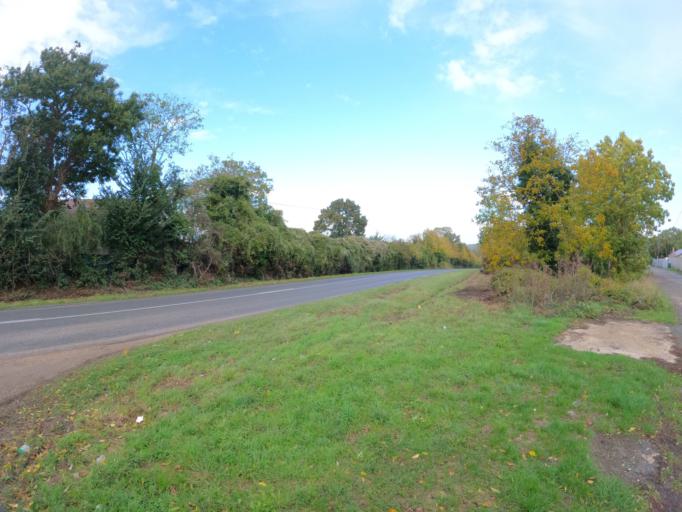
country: FR
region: Ile-de-France
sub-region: Departement de Seine-et-Marne
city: Saint-Germain-sur-Morin
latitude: 48.8721
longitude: 2.8532
